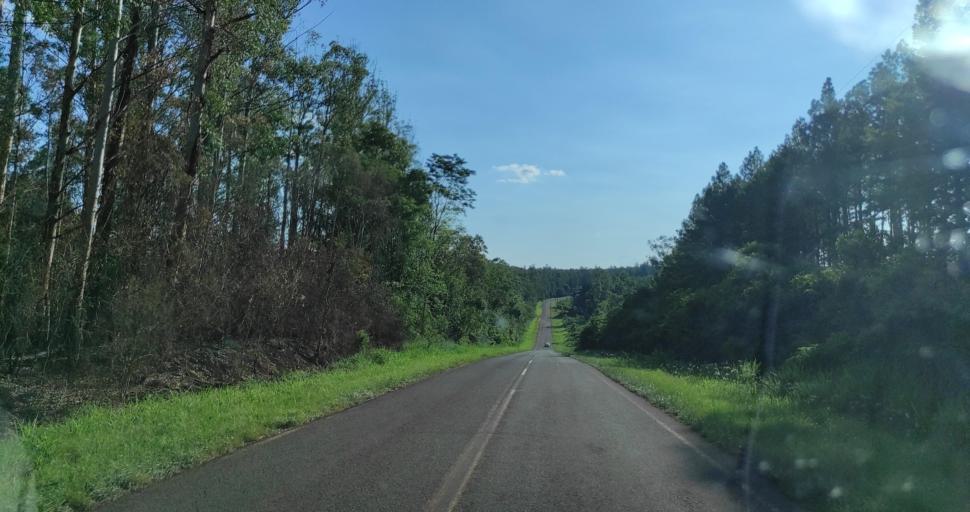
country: AR
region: Misiones
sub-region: Departamento de Eldorado
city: Eldorado
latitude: -26.3952
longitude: -54.3660
